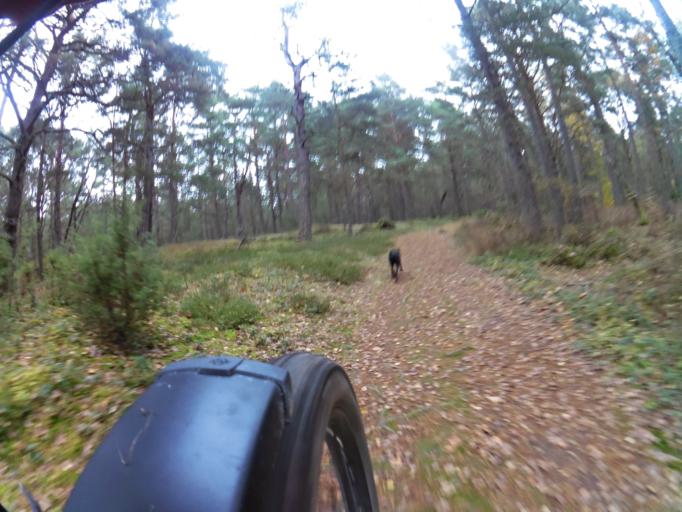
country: PL
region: Pomeranian Voivodeship
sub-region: Powiat leborski
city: Leba
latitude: 54.7754
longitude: 17.6768
